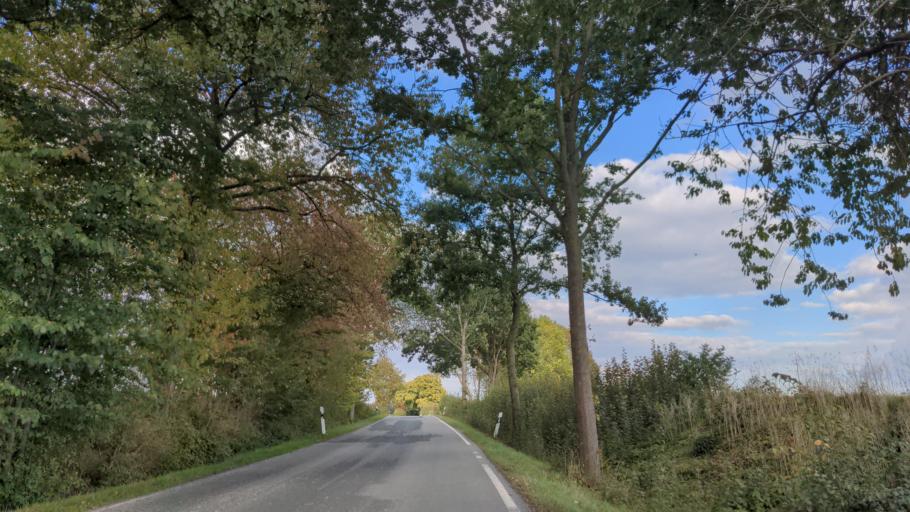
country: DE
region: Schleswig-Holstein
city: Ahrensbok
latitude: 53.9571
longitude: 10.5946
